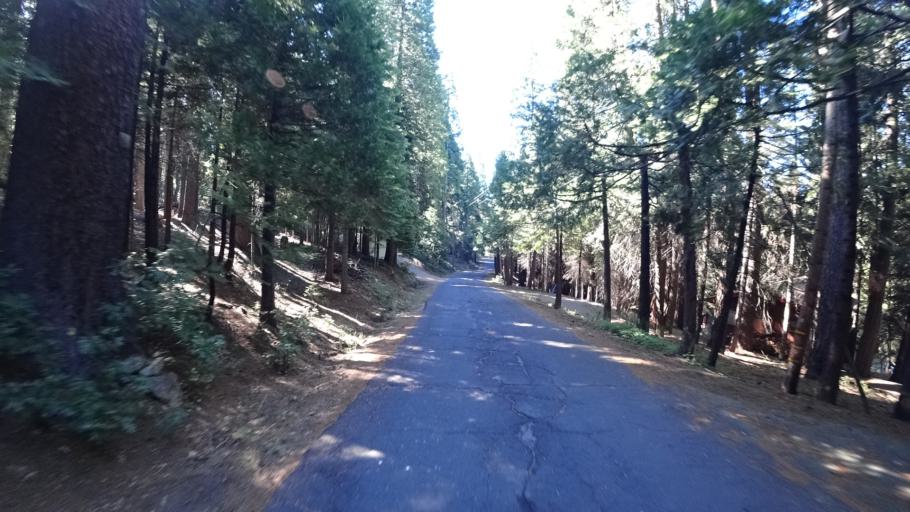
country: US
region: California
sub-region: Calaveras County
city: Arnold
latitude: 38.3028
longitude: -120.2747
